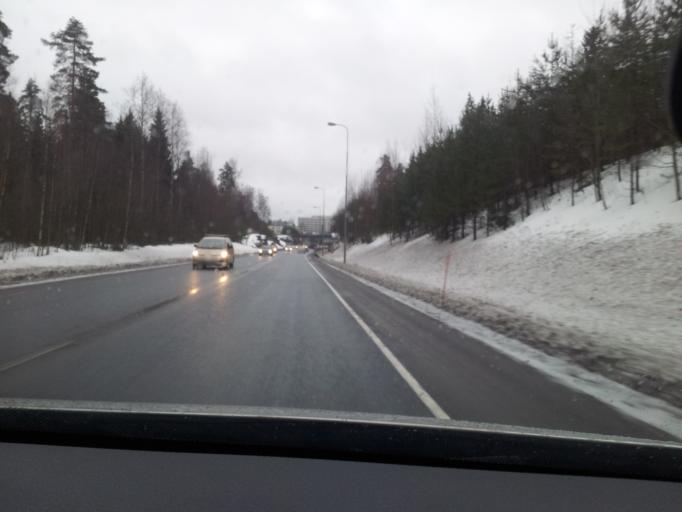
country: FI
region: Uusimaa
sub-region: Helsinki
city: Kauniainen
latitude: 60.2218
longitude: 24.7499
